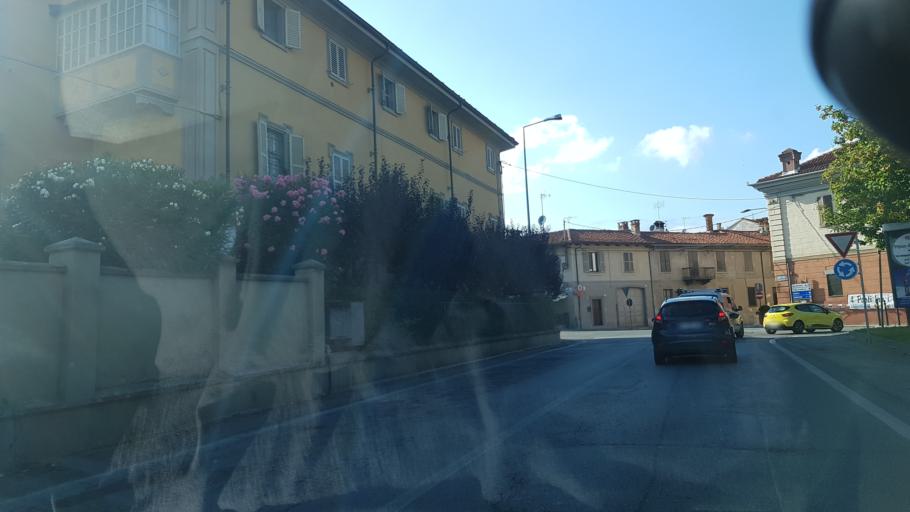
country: IT
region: Piedmont
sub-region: Provincia di Cuneo
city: Costiglione Saluzzo
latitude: 44.5622
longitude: 7.4864
